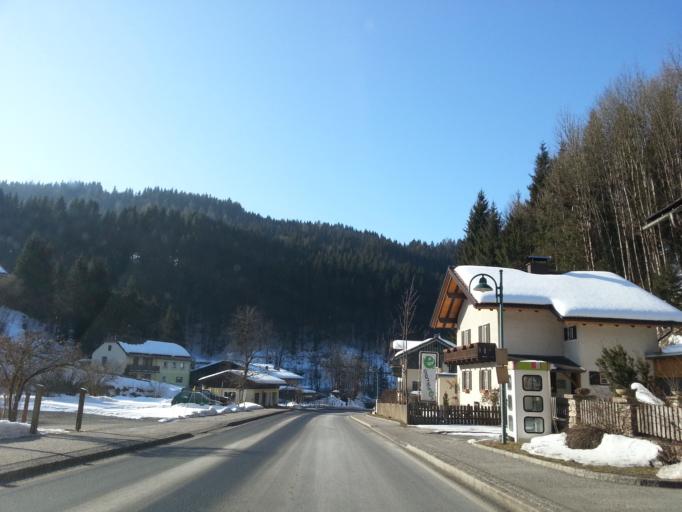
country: AT
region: Salzburg
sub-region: Politischer Bezirk Sankt Johann im Pongau
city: Huttau
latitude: 47.4232
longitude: 13.3459
